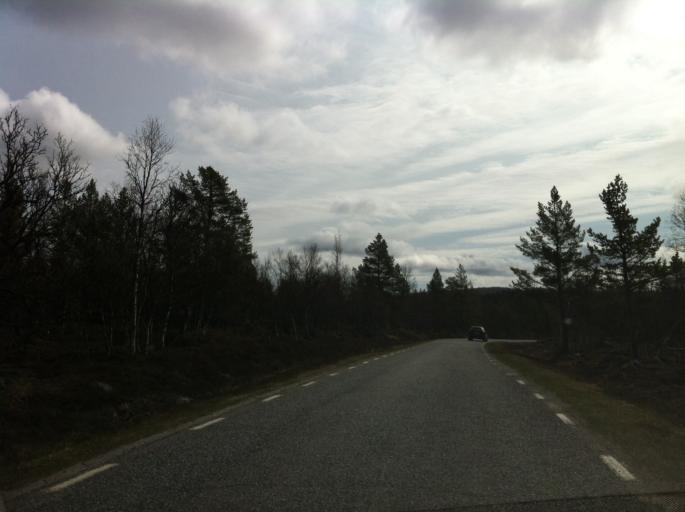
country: NO
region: Hedmark
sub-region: Engerdal
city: Engerdal
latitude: 62.3209
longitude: 12.8088
